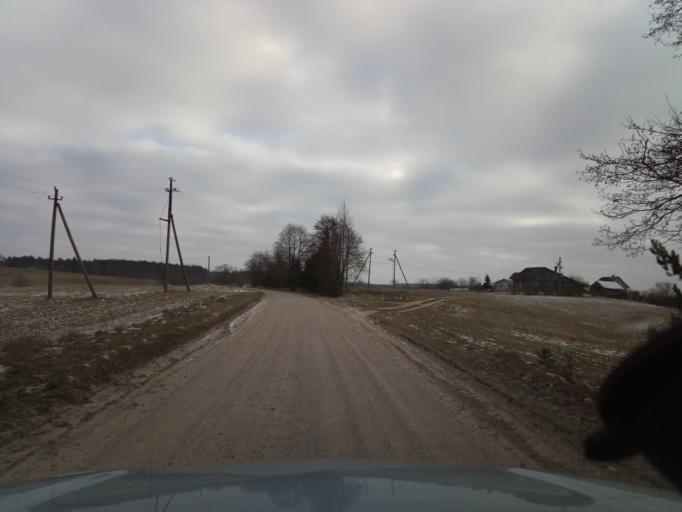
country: LT
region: Alytaus apskritis
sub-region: Alytaus rajonas
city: Daugai
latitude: 54.3179
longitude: 24.3385
